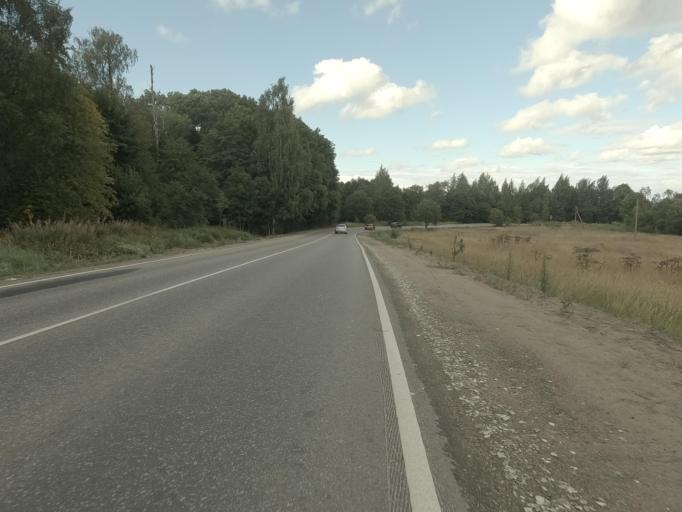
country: RU
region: Leningrad
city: Shcheglovo
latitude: 60.0281
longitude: 30.7649
